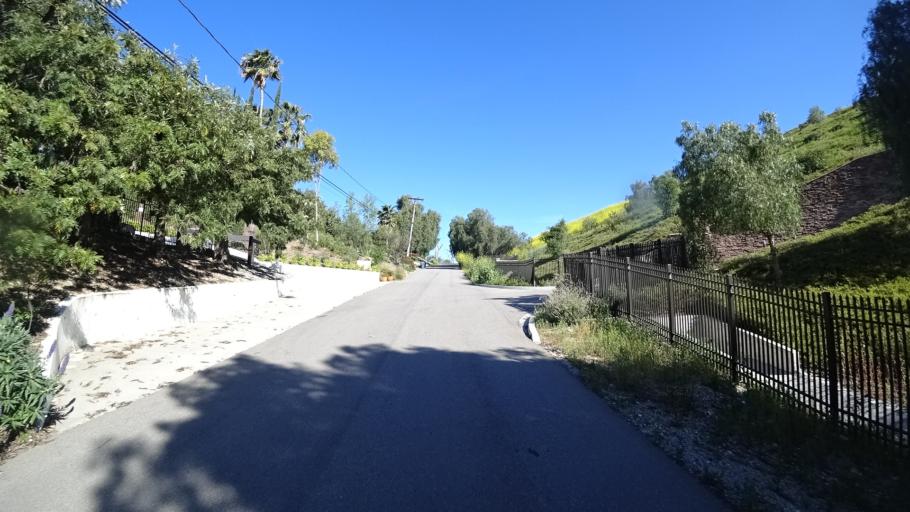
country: US
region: California
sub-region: Ventura County
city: Thousand Oaks
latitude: 34.1832
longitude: -118.8448
